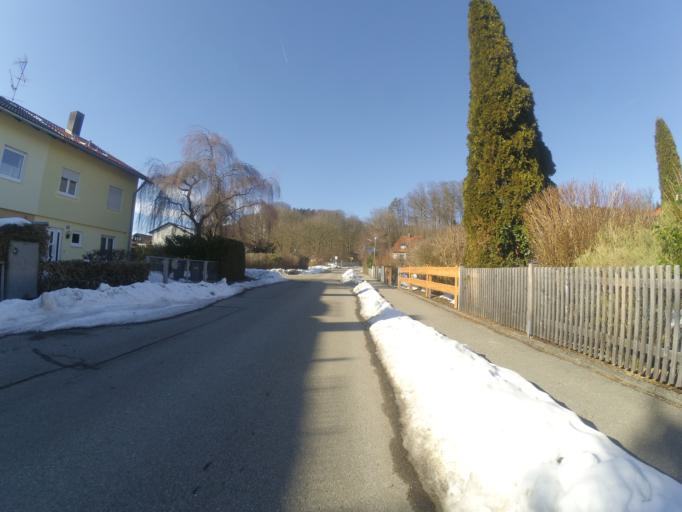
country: DE
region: Bavaria
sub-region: Upper Bavaria
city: Feldkirchen-Westerham
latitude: 47.9058
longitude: 11.8330
